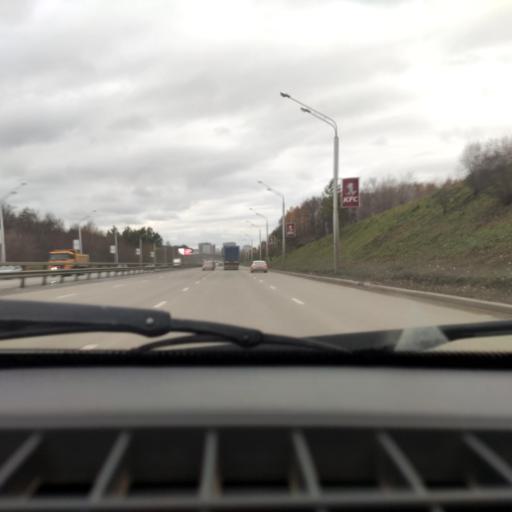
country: RU
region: Bashkortostan
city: Ufa
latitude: 54.7462
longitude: 56.0134
